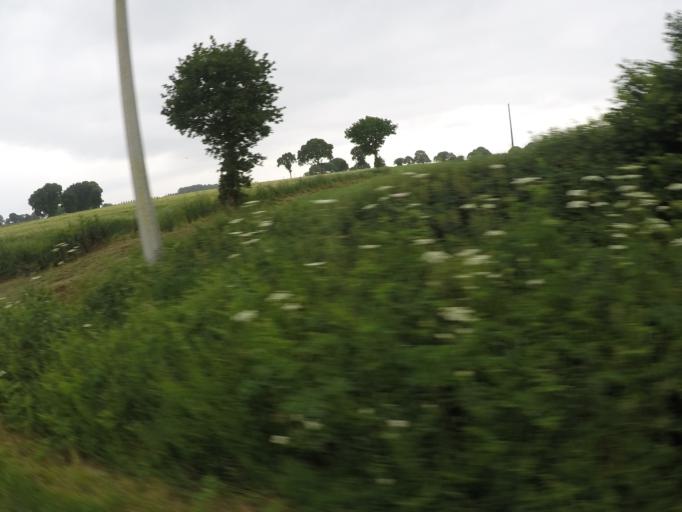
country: FR
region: Brittany
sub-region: Departement des Cotes-d'Armor
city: Goudelin
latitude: 48.6238
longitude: -3.0443
